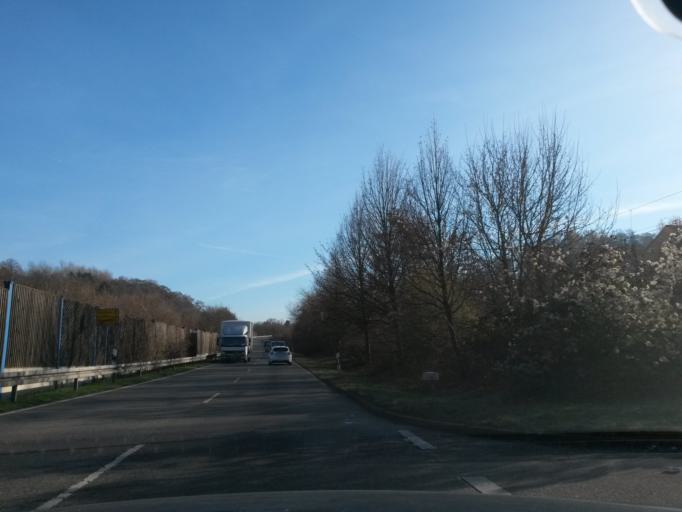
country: DE
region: Baden-Wuerttemberg
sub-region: Karlsruhe Region
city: Ispringen
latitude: 48.9141
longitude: 8.6732
